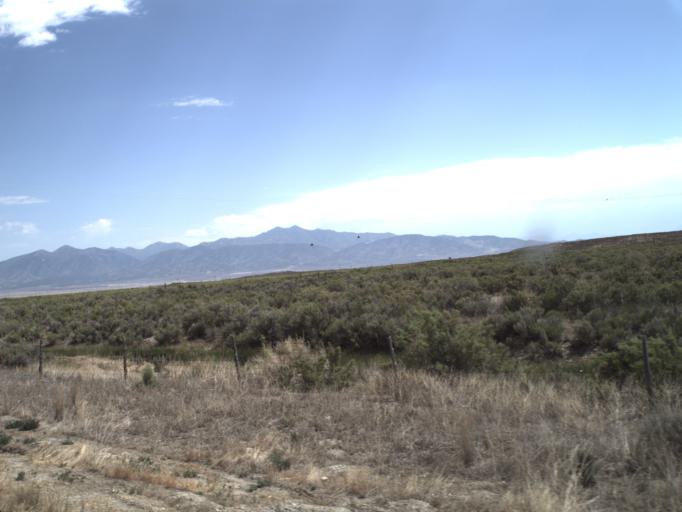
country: US
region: Utah
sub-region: Tooele County
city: Tooele
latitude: 40.1585
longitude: -112.4307
